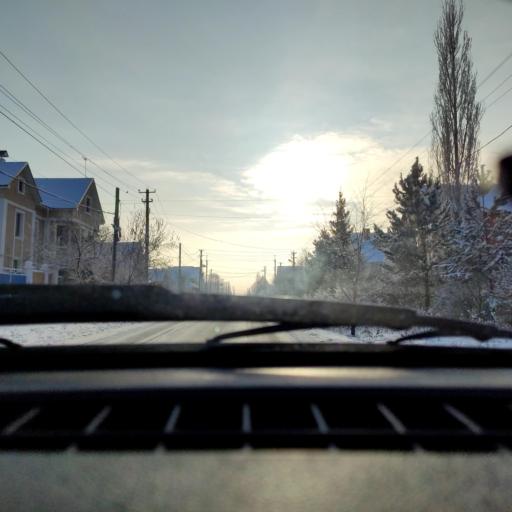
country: RU
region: Bashkortostan
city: Ufa
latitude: 54.6001
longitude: 55.9355
